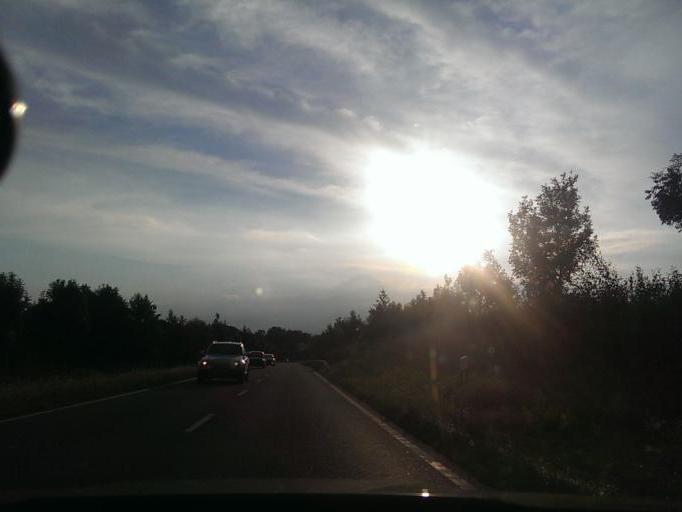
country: DE
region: Lower Saxony
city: Lilienthal
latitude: 53.1593
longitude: 8.9089
